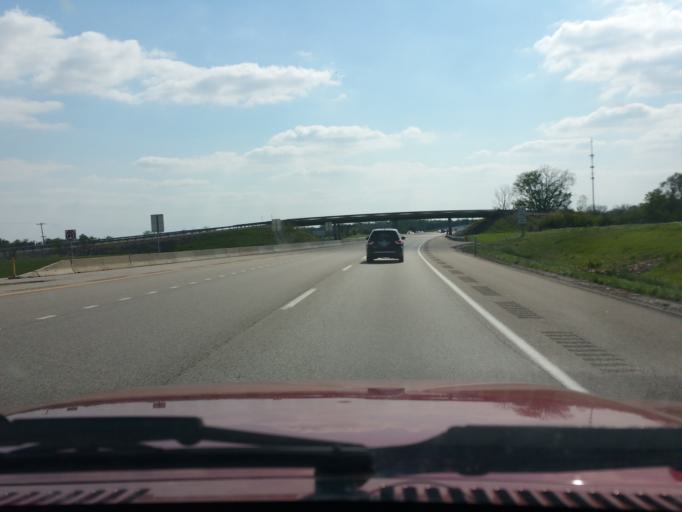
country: US
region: Kansas
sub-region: Douglas County
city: Eudora
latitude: 39.0162
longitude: -95.1420
